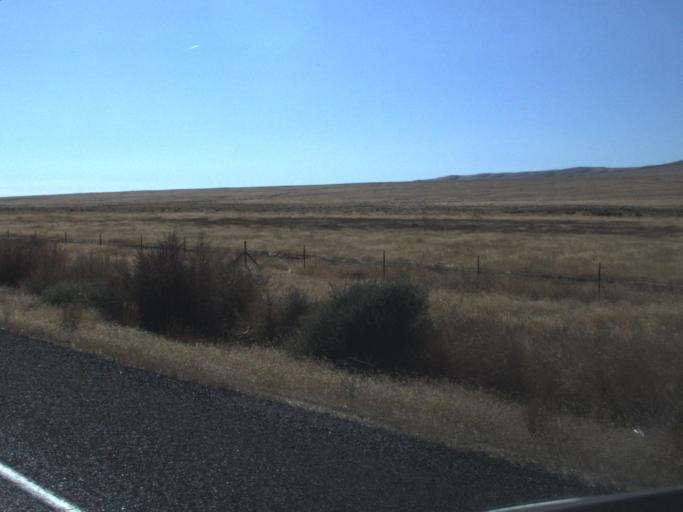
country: US
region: Washington
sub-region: Benton County
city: Benton City
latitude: 46.4733
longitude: -119.5546
